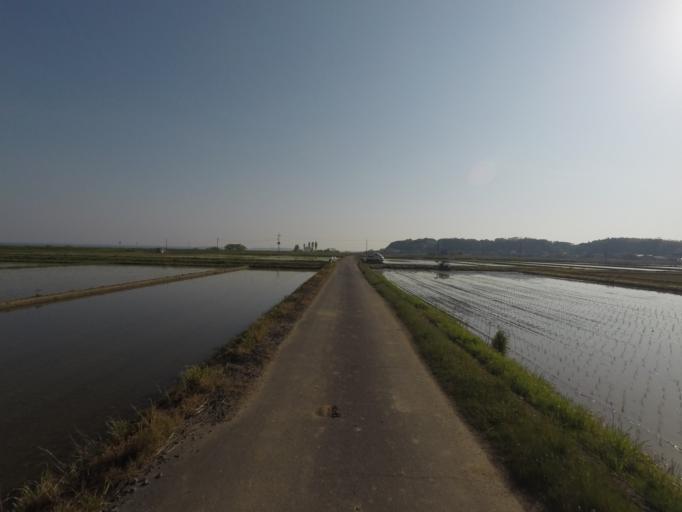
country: JP
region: Ibaraki
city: Inashiki
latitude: 36.0792
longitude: 140.3840
